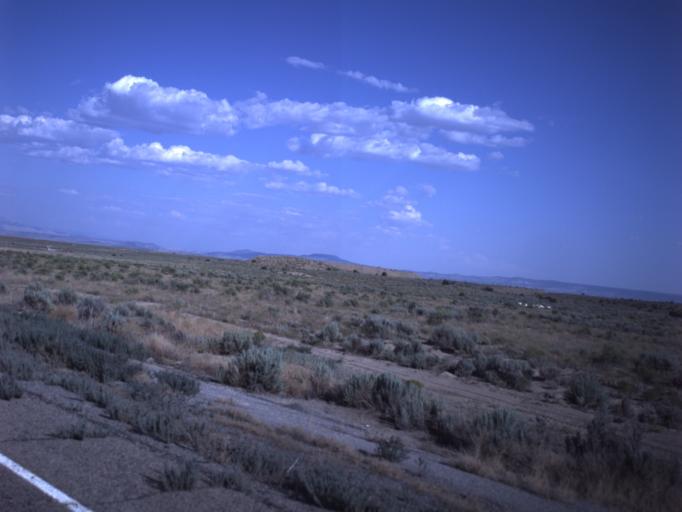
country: US
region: Utah
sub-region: Carbon County
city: Price
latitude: 39.4841
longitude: -110.8890
